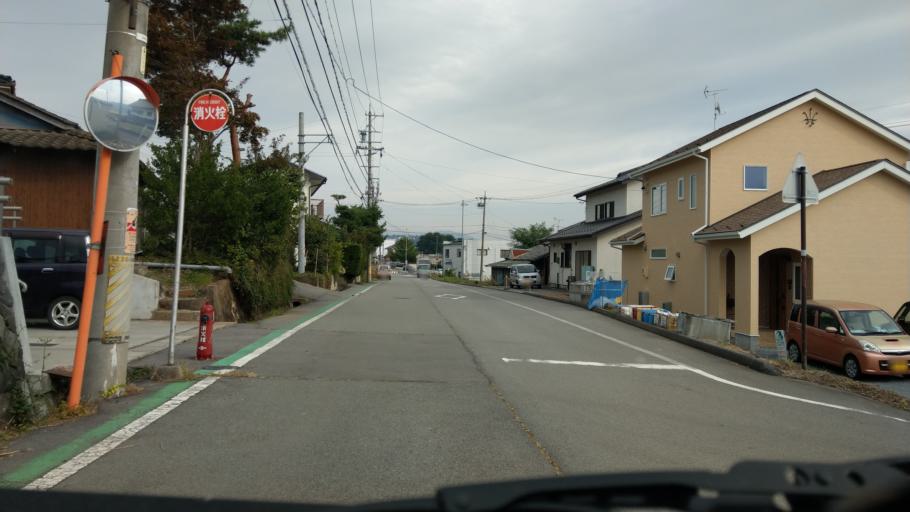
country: JP
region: Nagano
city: Komoro
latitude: 36.3384
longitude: 138.4046
